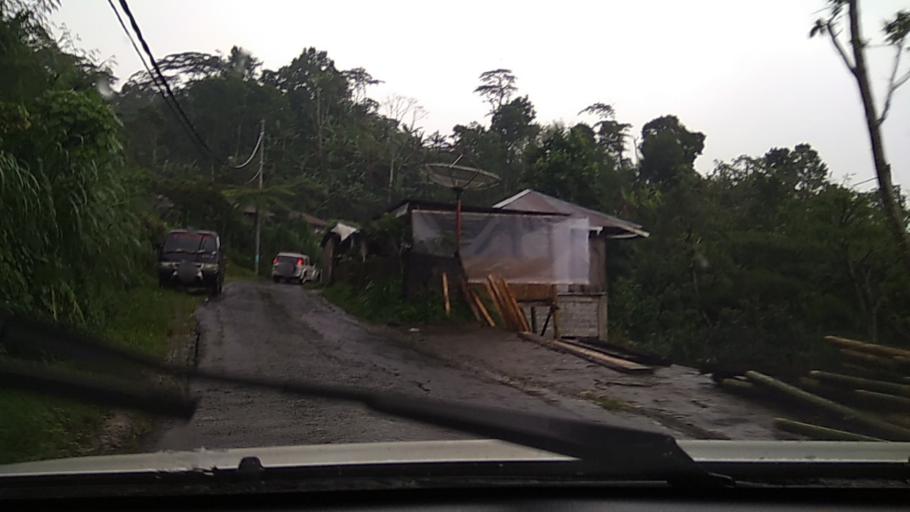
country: ID
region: Bali
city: Banjar Ambengan
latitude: -8.2238
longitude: 115.1591
